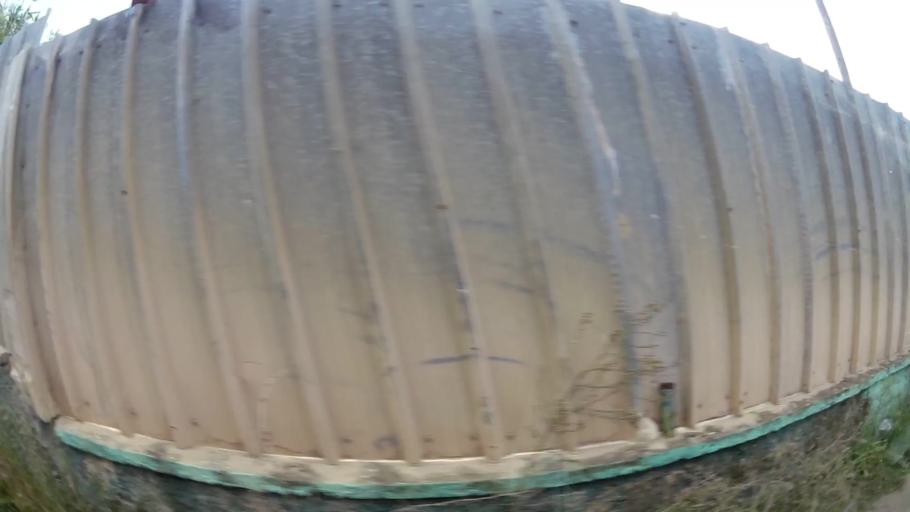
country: GR
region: Attica
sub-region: Nomarchia Anatolikis Attikis
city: Acharnes
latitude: 38.0991
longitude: 23.7527
